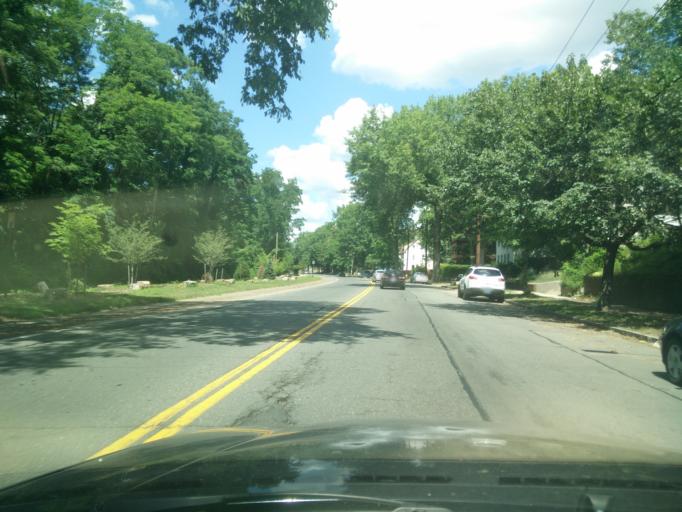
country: US
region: Connecticut
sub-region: New Haven County
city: New Haven
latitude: 41.3259
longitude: -72.9368
